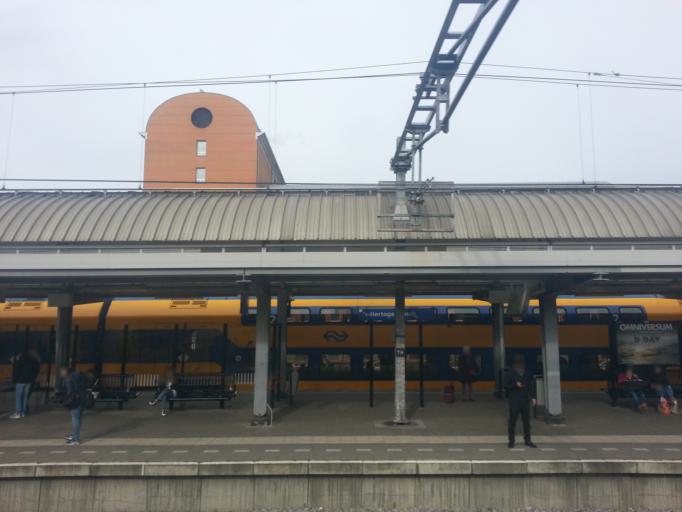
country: NL
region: North Brabant
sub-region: Gemeente 's-Hertogenbosch
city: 's-Hertogenbosch
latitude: 51.6894
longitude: 5.2931
